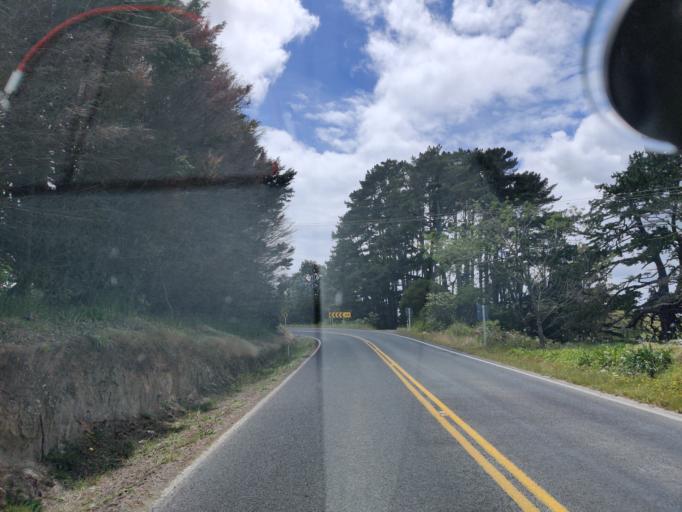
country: NZ
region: Northland
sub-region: Far North District
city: Kaitaia
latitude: -34.9969
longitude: 173.1936
